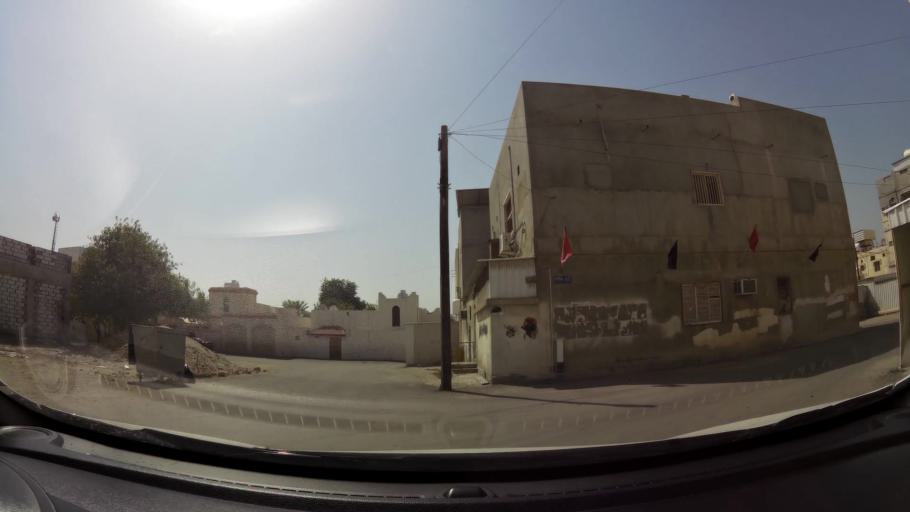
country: BH
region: Manama
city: Jidd Hafs
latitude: 26.1971
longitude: 50.4632
